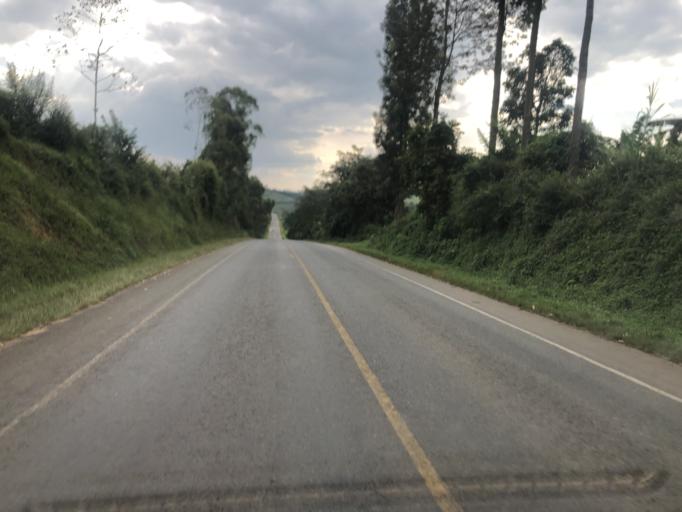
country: UG
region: Western Region
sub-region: Sheema District
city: Kibingo
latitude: -0.5613
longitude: 30.3366
